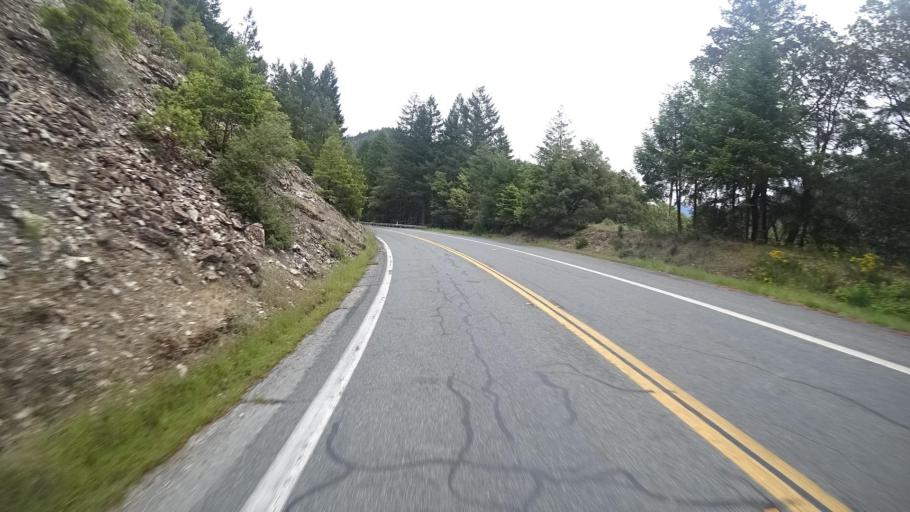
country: US
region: California
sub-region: Humboldt County
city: Willow Creek
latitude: 41.2600
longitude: -123.6081
